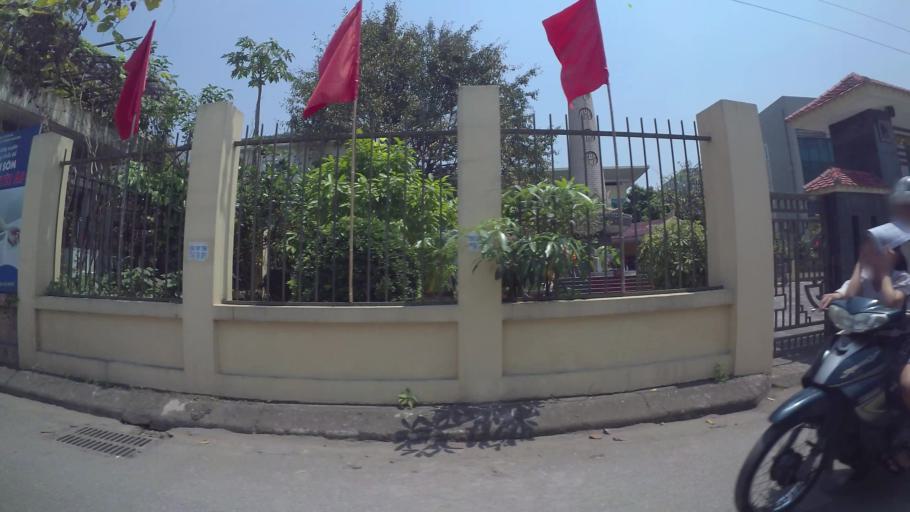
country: VN
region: Ha Noi
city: Hoan Kiem
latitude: 21.0380
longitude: 105.8715
